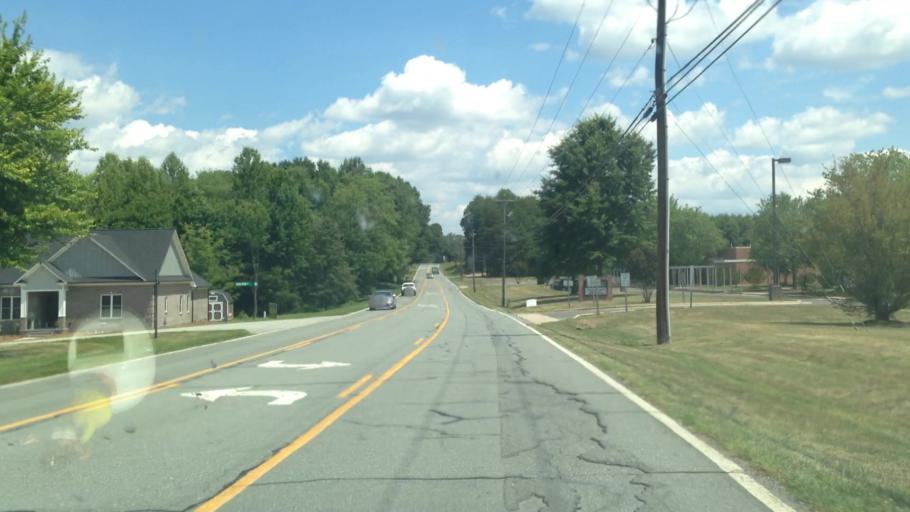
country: US
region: North Carolina
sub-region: Forsyth County
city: Kernersville
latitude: 36.1591
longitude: -80.0556
